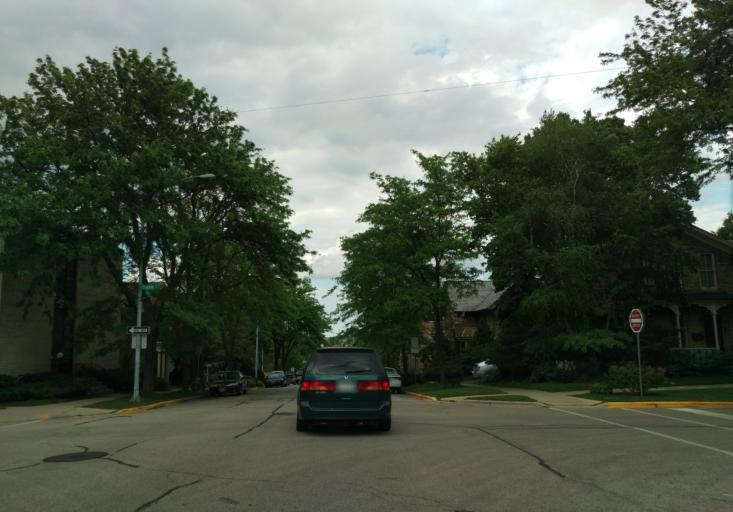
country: US
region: Wisconsin
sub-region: Dane County
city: Madison
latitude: 43.0770
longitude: -89.3786
